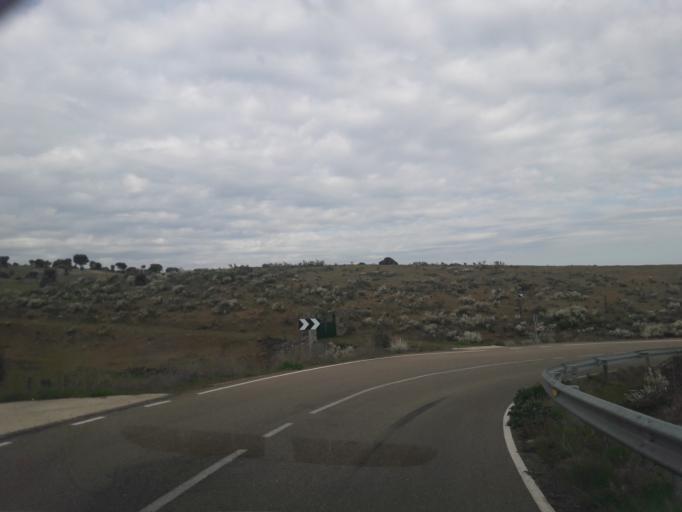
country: ES
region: Castille and Leon
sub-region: Provincia de Salamanca
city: Pastores
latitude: 40.5184
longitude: -6.5152
